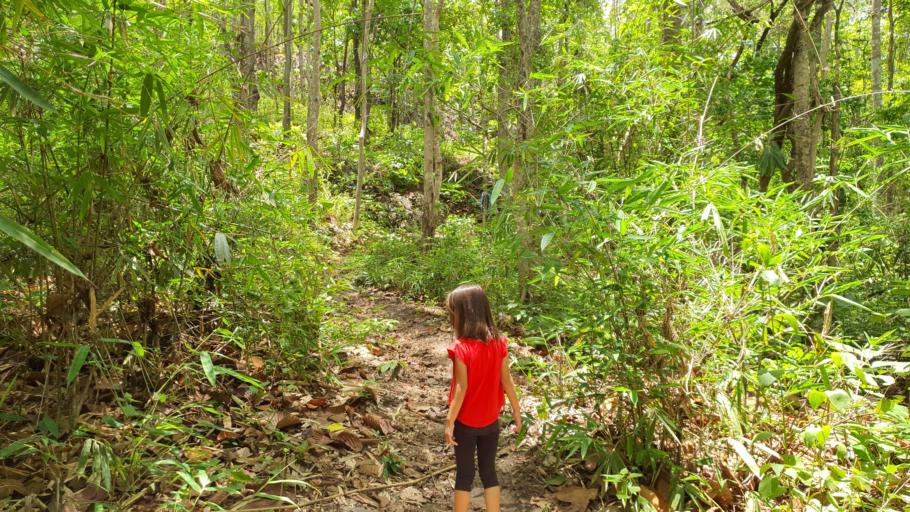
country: TH
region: Chiang Mai
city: San Sai
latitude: 18.9429
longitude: 99.0658
